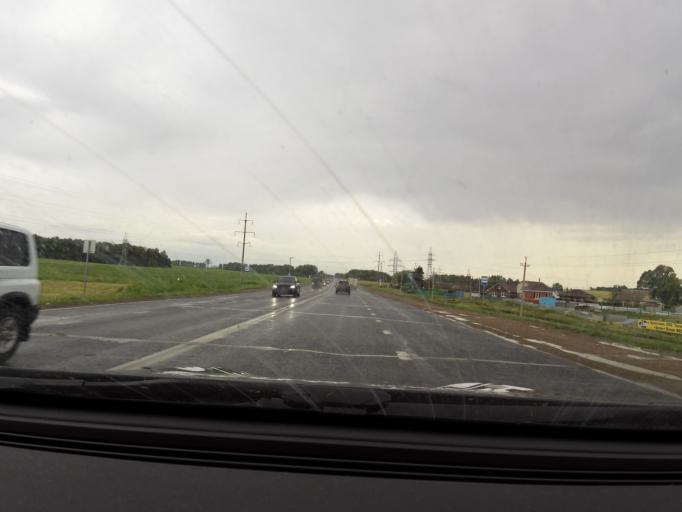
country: RU
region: Bashkortostan
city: Mikhaylovka
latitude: 54.8141
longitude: 55.8448
